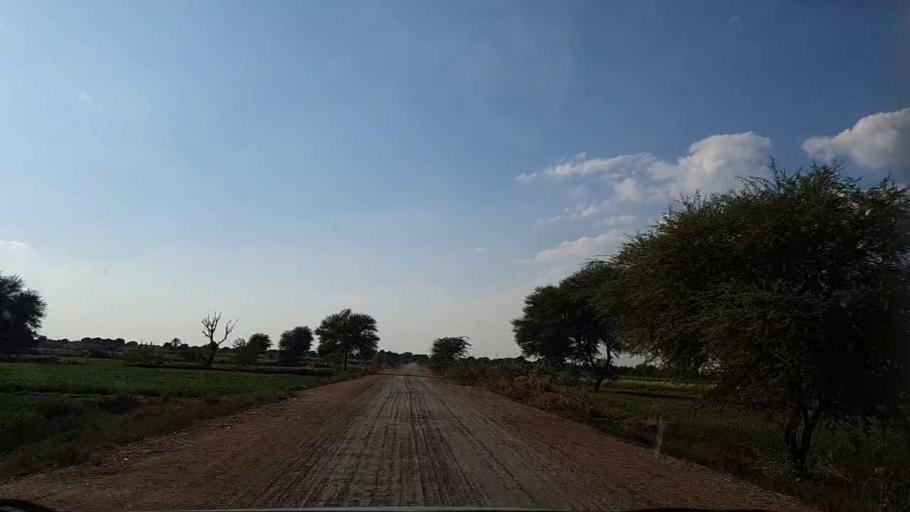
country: PK
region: Sindh
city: Pithoro
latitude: 25.6495
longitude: 69.2921
